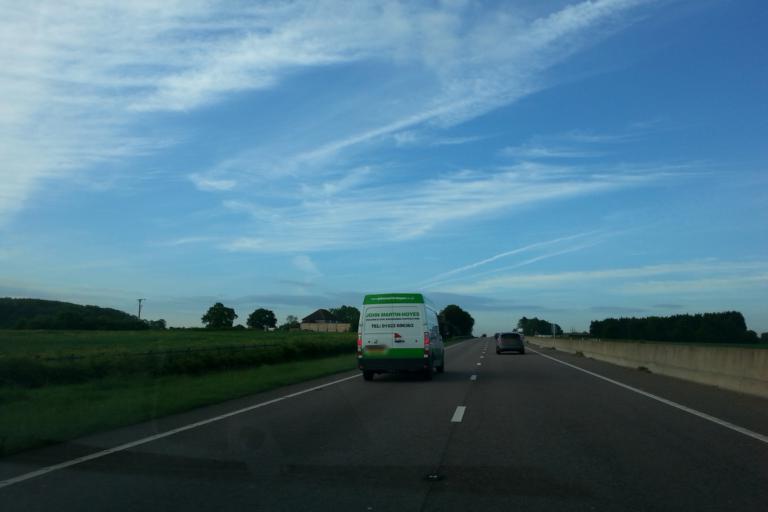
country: GB
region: England
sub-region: Nottinghamshire
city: Cotgrave
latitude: 52.8779
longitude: -1.0273
